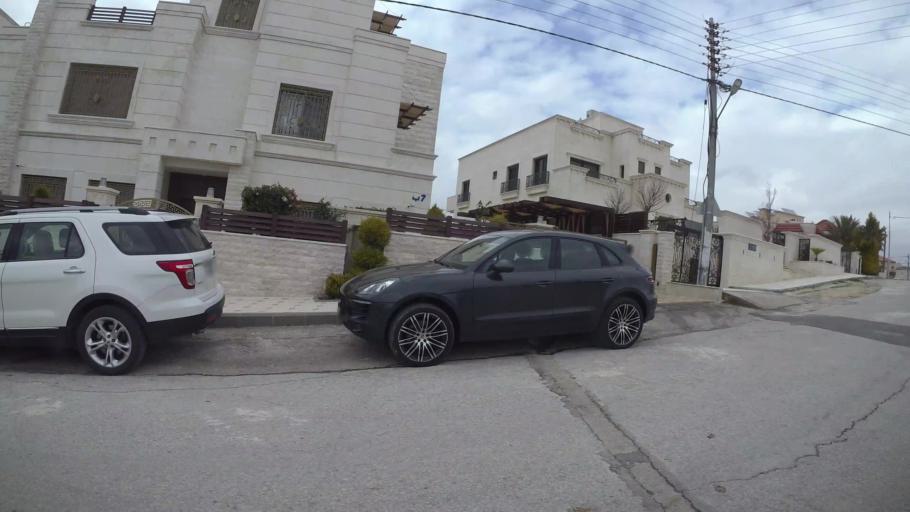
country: JO
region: Amman
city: Wadi as Sir
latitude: 31.9883
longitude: 35.8336
